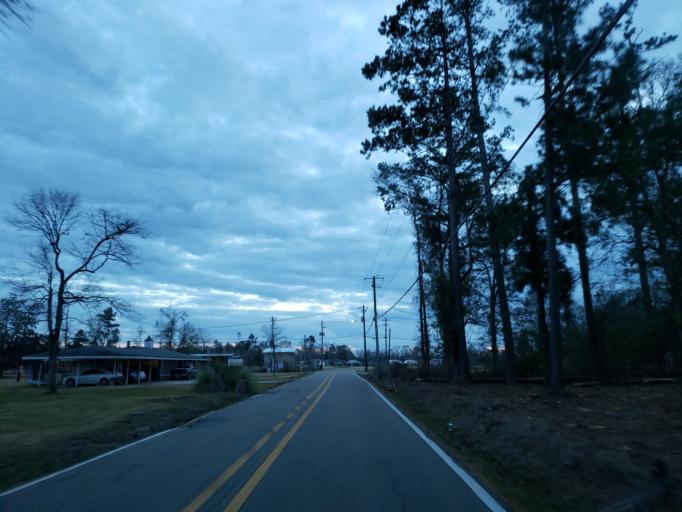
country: US
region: Mississippi
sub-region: Forrest County
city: Petal
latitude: 31.3334
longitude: -89.2603
